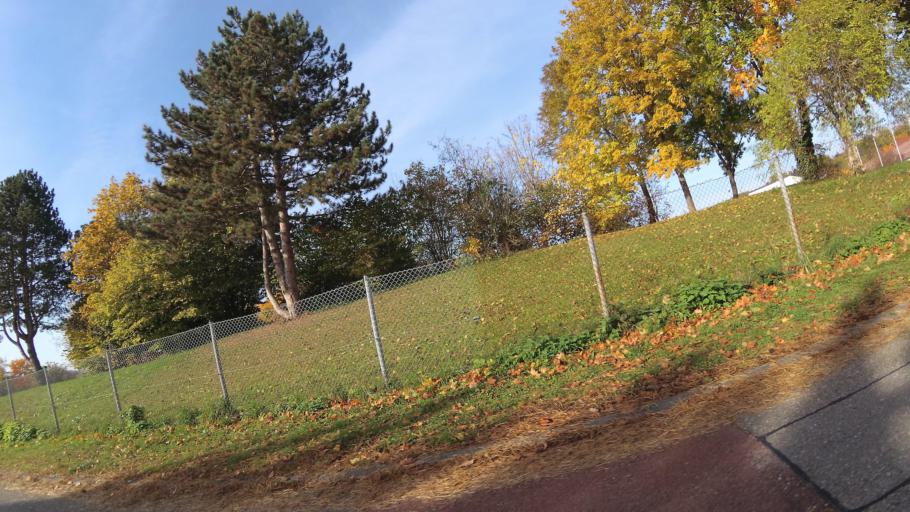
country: DE
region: Baden-Wuerttemberg
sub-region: Regierungsbezirk Stuttgart
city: Oedheim
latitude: 49.2433
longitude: 9.2435
